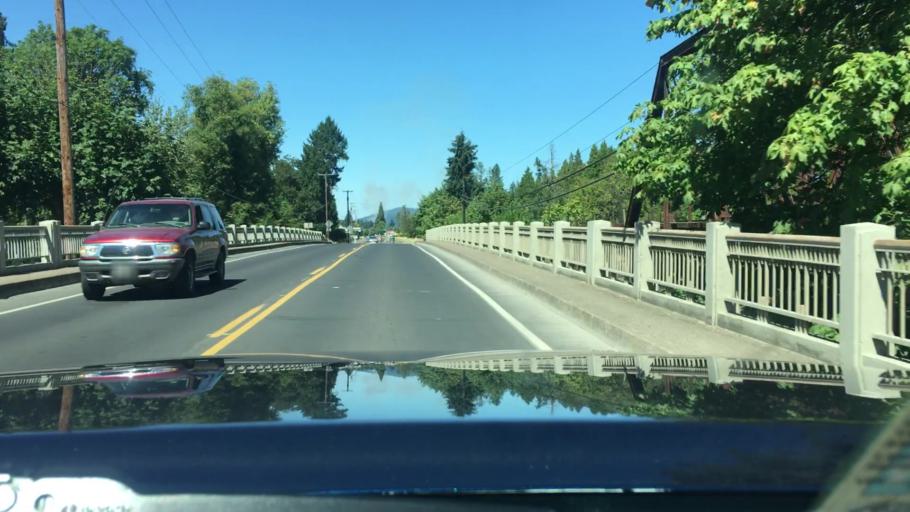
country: US
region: Oregon
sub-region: Lane County
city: Cottage Grove
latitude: 43.7842
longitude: -123.0685
